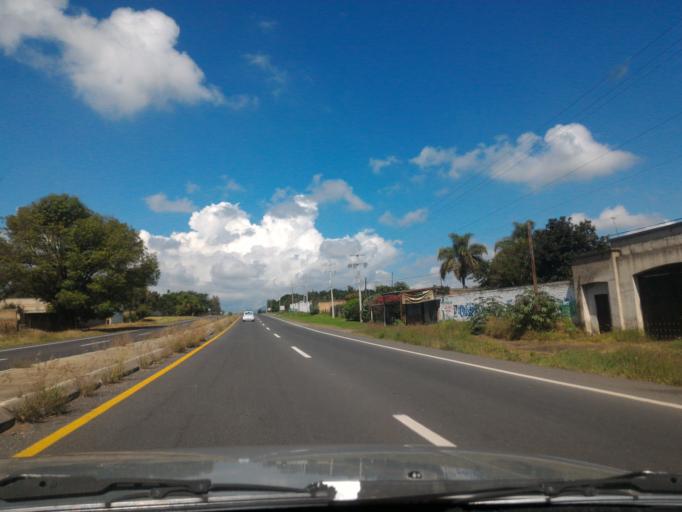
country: MX
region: Jalisco
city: Arenal
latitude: 20.7496
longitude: -103.6491
